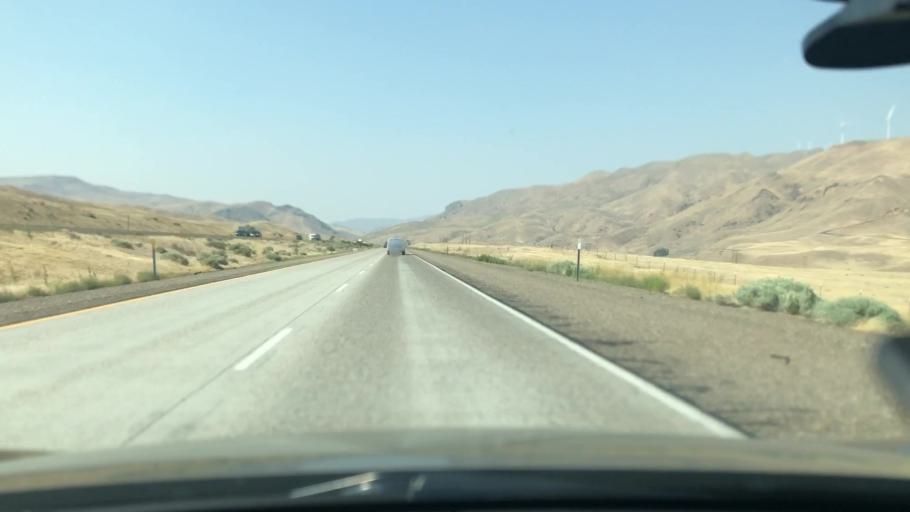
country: US
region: Idaho
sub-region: Washington County
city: Weiser
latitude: 44.3498
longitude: -117.2890
